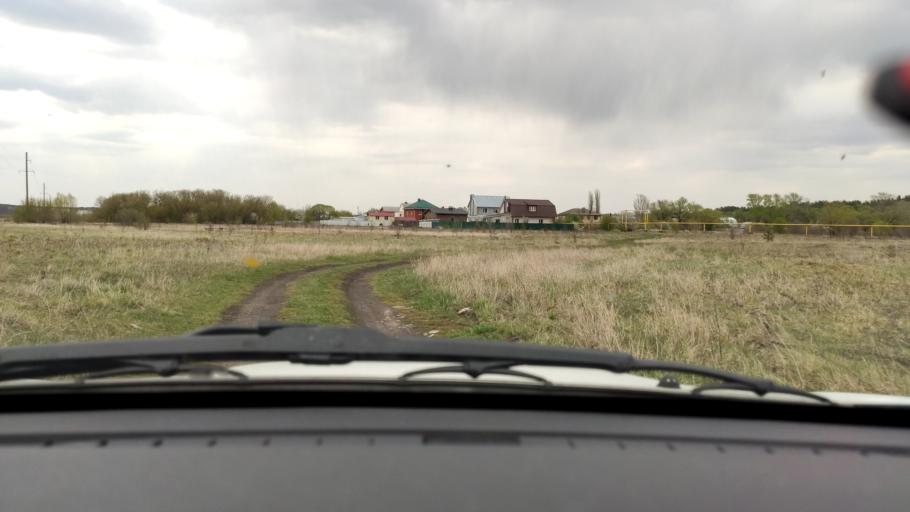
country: RU
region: Voronezj
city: Somovo
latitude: 51.7368
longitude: 39.3362
